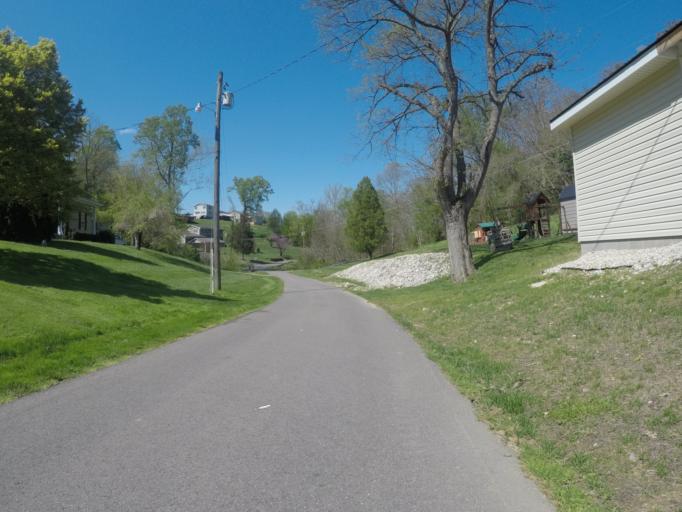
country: US
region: West Virginia
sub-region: Wayne County
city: Kenova
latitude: 38.3954
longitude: -82.5878
